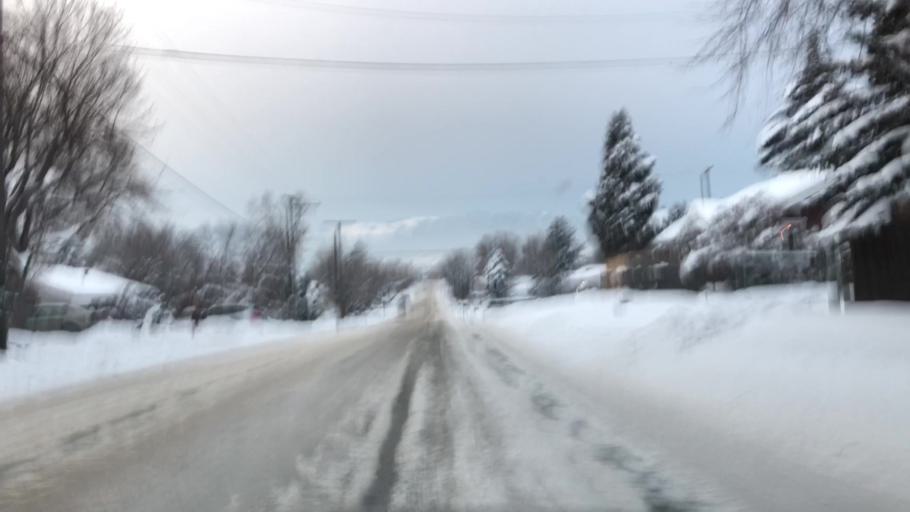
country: US
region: Montana
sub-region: Lewis and Clark County
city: Helena
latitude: 46.6083
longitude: -112.0266
